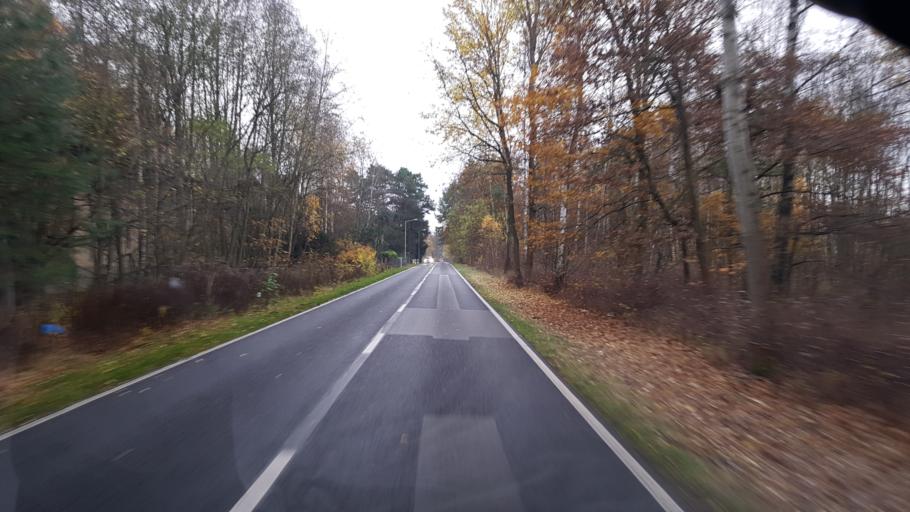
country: DE
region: Brandenburg
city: Lauchhammer
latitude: 51.4955
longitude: 13.7263
